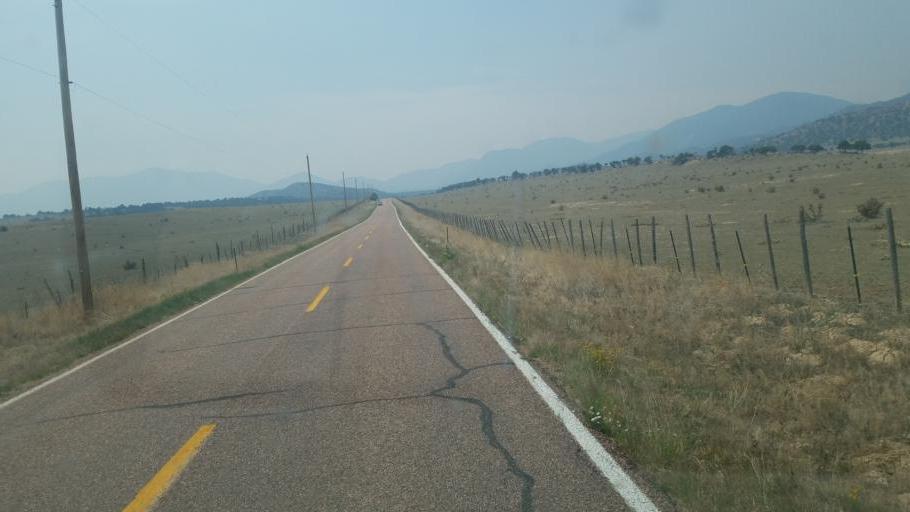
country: US
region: Colorado
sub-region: Fremont County
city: Canon City
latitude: 38.4624
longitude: -105.3764
